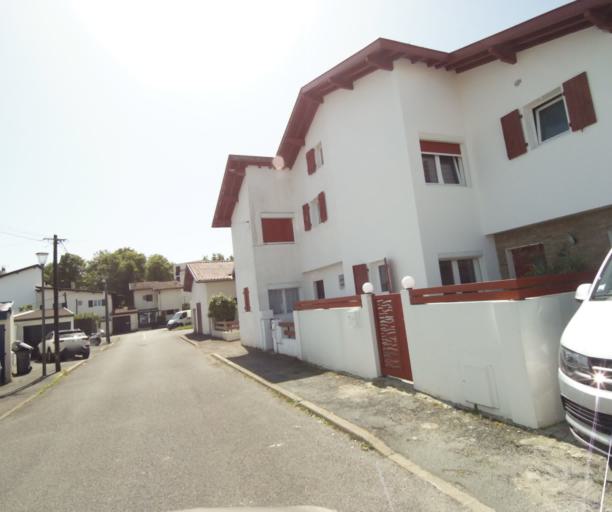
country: FR
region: Aquitaine
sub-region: Departement des Pyrenees-Atlantiques
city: Bayonne
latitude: 43.4763
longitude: -1.4609
